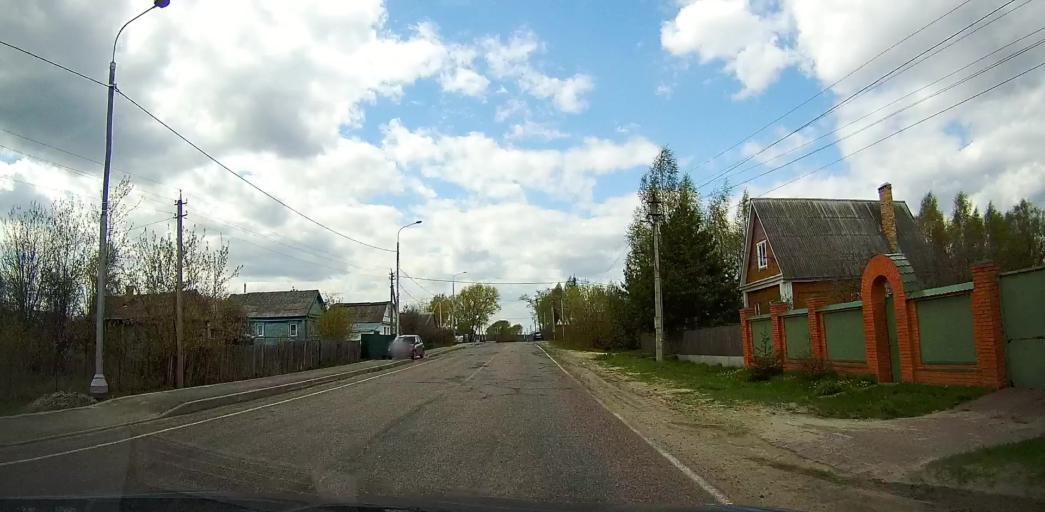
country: RU
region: Moskovskaya
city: Drezna
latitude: 55.6713
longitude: 38.7709
